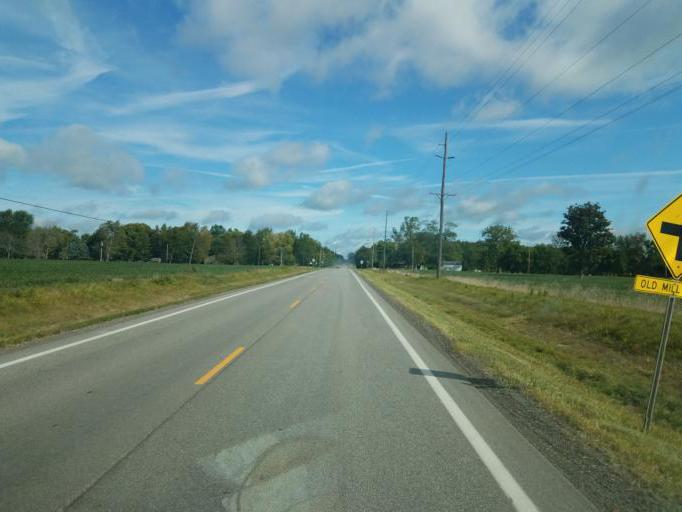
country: US
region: Ohio
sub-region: Wayne County
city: West Salem
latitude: 41.0835
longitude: -82.1236
